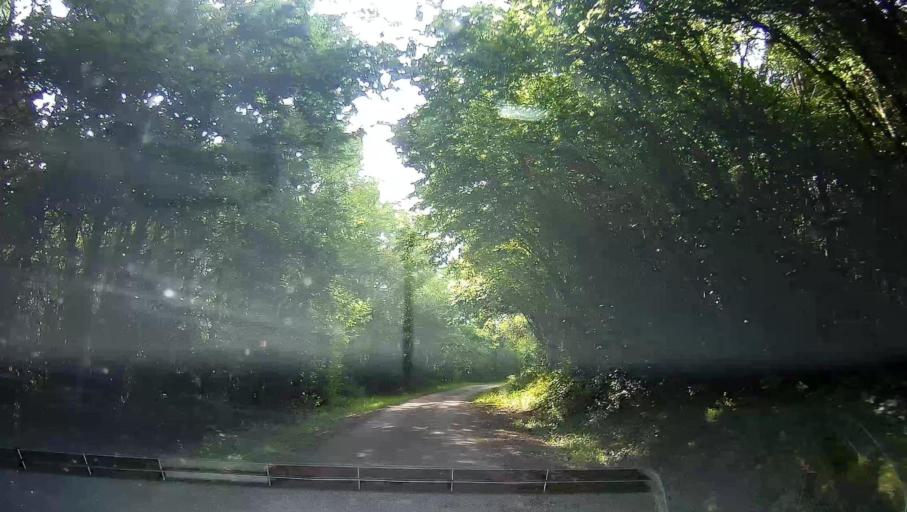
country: FR
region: Bourgogne
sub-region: Departement de la Cote-d'Or
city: Nolay
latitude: 46.9038
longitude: 4.6132
